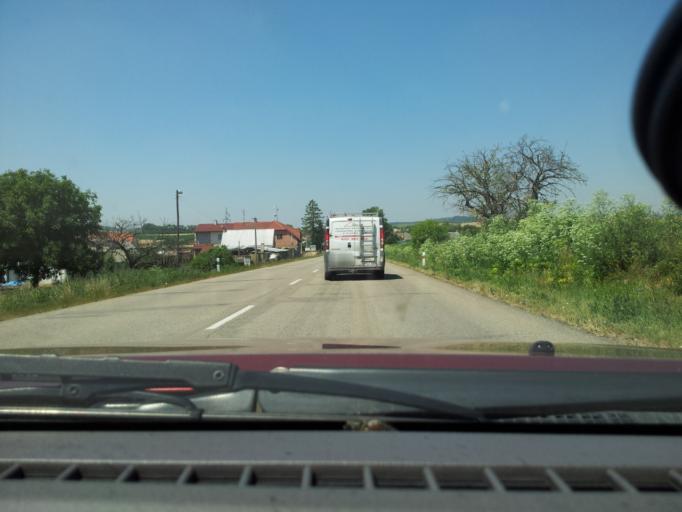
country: CZ
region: South Moravian
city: Krumvir
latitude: 48.9802
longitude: 16.9256
